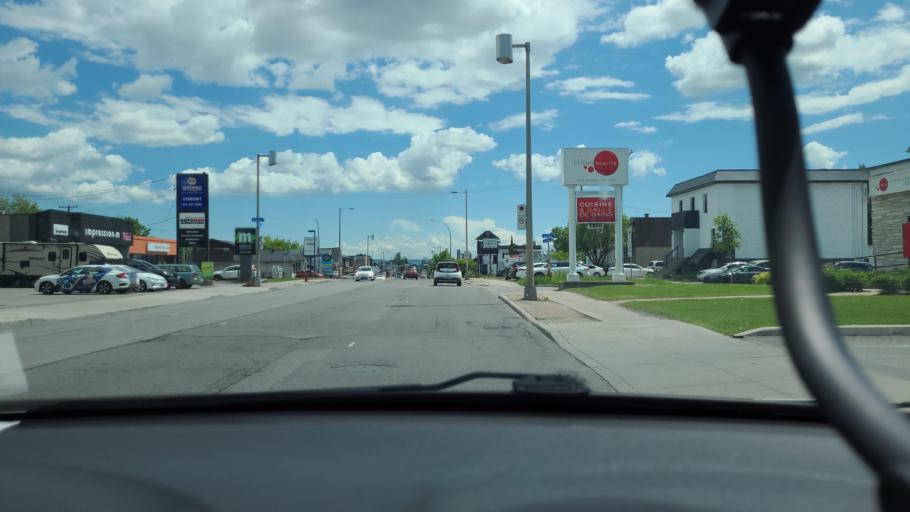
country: CA
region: Quebec
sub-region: Laval
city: Laval
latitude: 45.6015
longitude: -73.7269
